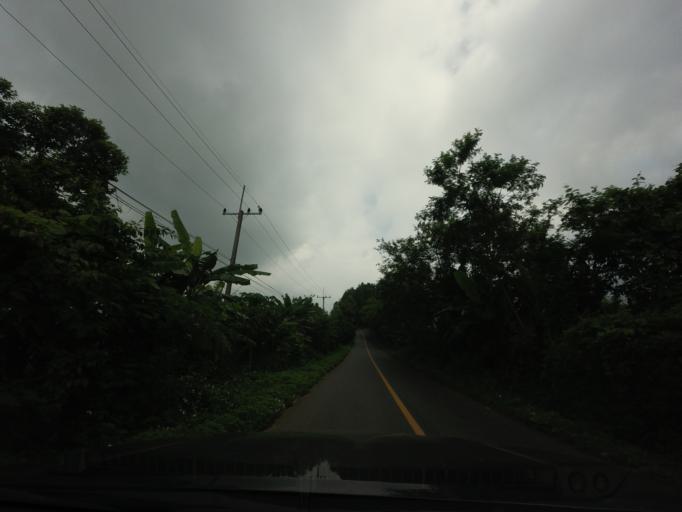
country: TH
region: Nan
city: Pua
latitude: 19.1883
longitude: 101.0330
